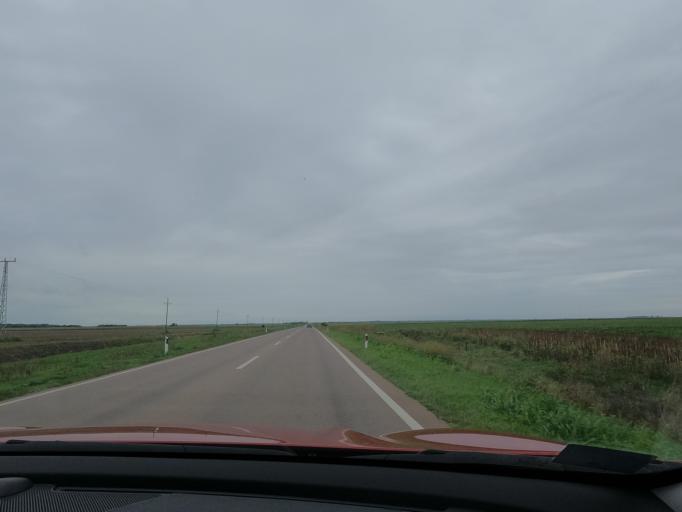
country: RS
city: Banatska Topola
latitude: 45.7335
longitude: 20.4198
